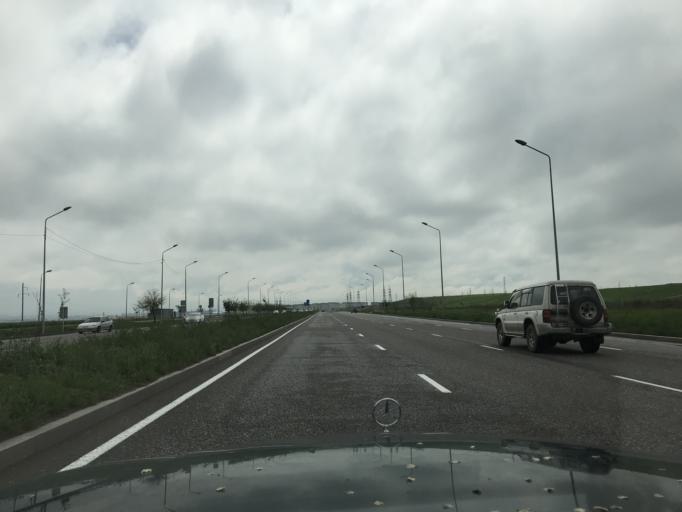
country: KZ
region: Almaty Oblysy
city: Burunday
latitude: 43.2953
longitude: 76.8322
